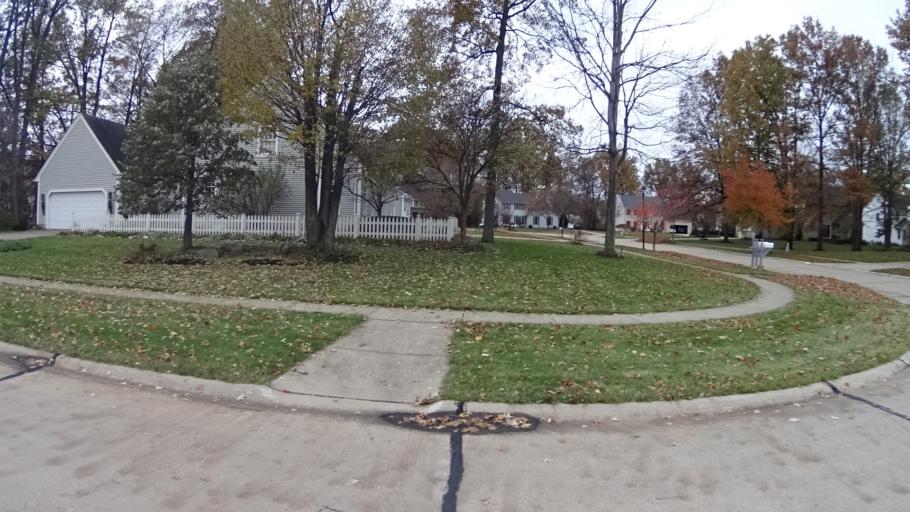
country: US
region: Ohio
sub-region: Lorain County
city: Avon Center
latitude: 41.4832
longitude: -81.9914
